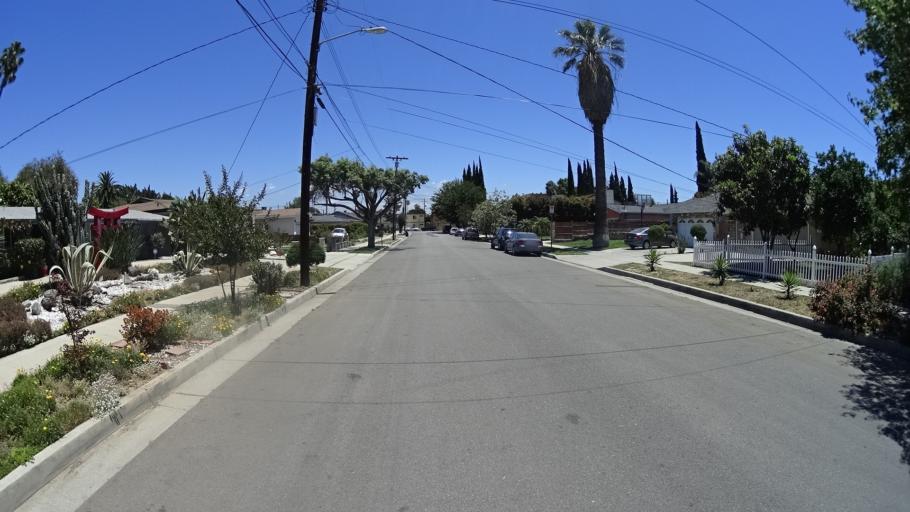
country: US
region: California
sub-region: Los Angeles County
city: Van Nuys
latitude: 34.2039
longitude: -118.4686
